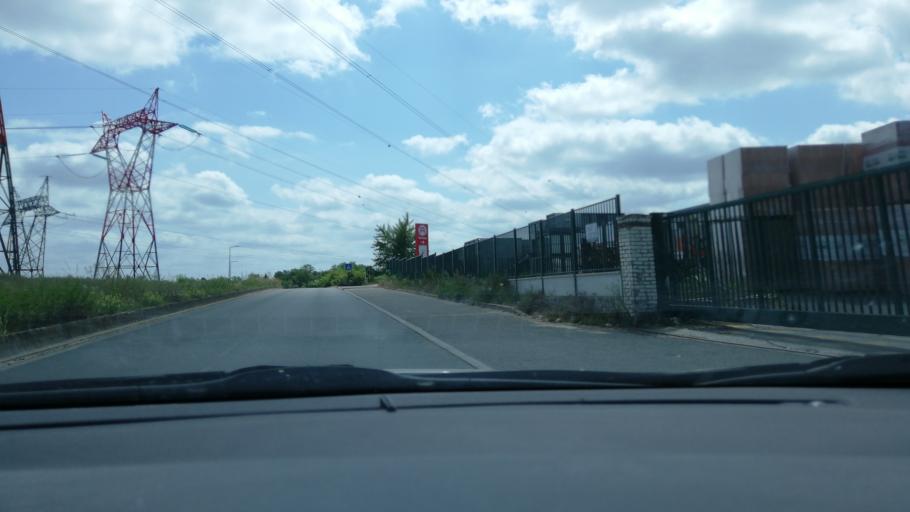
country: FR
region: Ile-de-France
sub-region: Departement du Val-d'Oise
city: Vaureal
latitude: 49.0656
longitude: 2.0218
